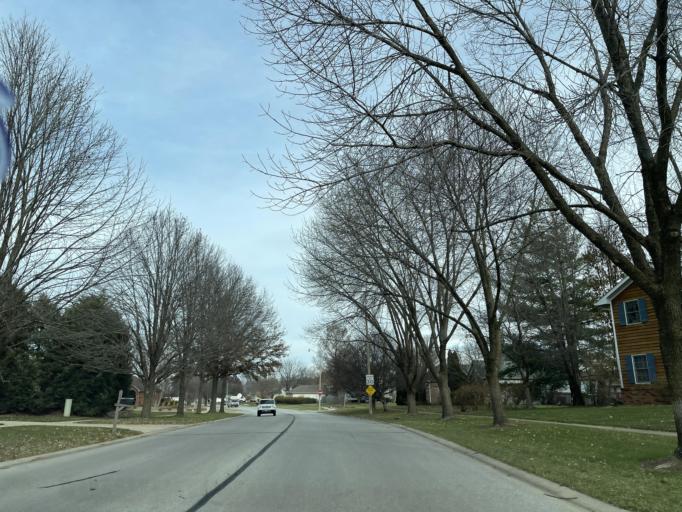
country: US
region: Illinois
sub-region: Sangamon County
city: Leland Grove
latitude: 39.7813
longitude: -89.7292
